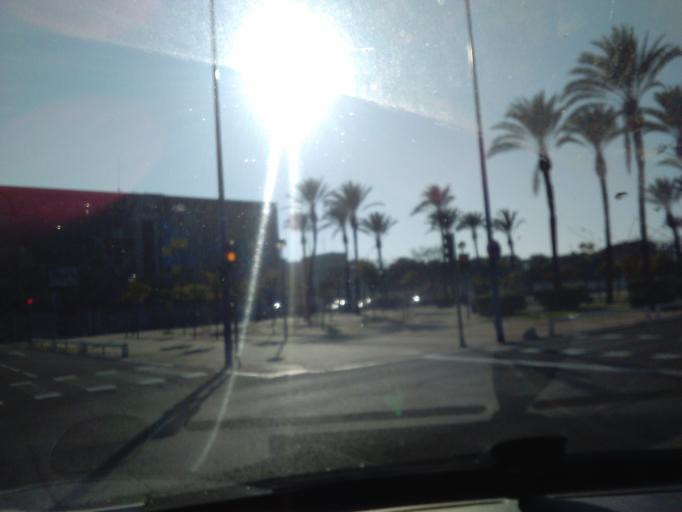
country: ES
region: Andalusia
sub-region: Provincia de Sevilla
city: Camas
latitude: 37.4065
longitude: -6.0069
